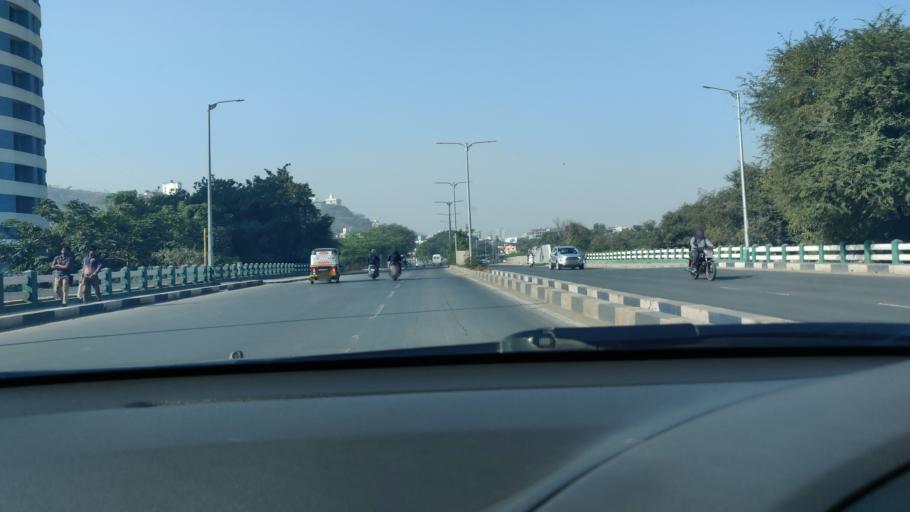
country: IN
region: Maharashtra
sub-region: Pune Division
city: Khadki
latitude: 18.5627
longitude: 73.7950
